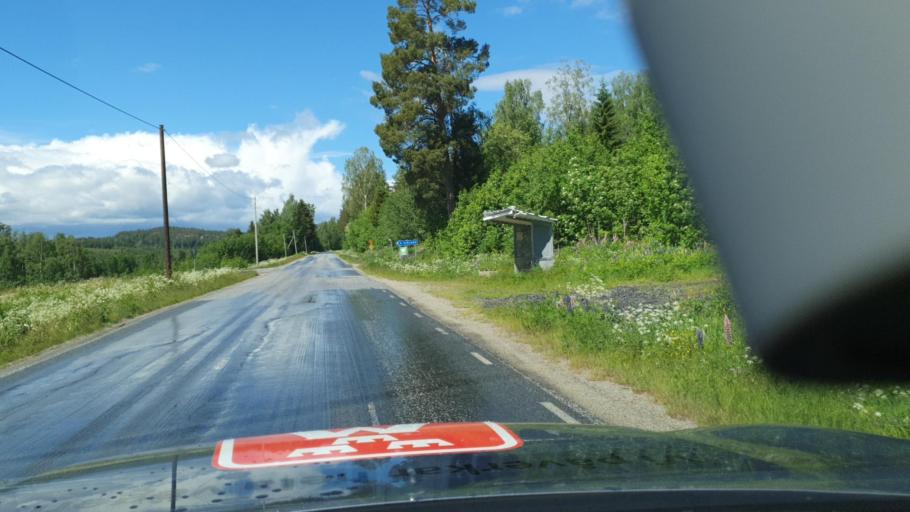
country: SE
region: Vaesternorrland
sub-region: OErnskoeldsviks Kommun
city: Bredbyn
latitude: 63.3392
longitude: 18.0162
